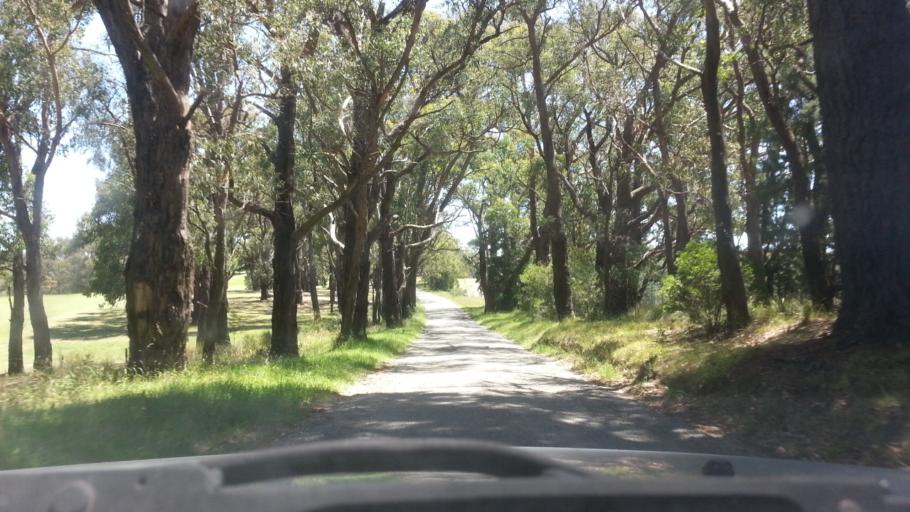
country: AU
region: Victoria
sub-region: Cardinia
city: Beaconsfield Upper
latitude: -37.9793
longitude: 145.4246
